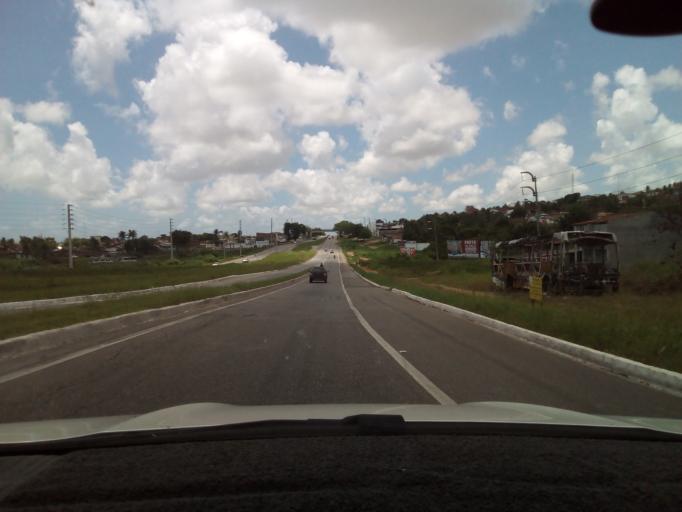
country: BR
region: Paraiba
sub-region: Bayeux
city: Bayeux
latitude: -7.1255
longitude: -34.9446
